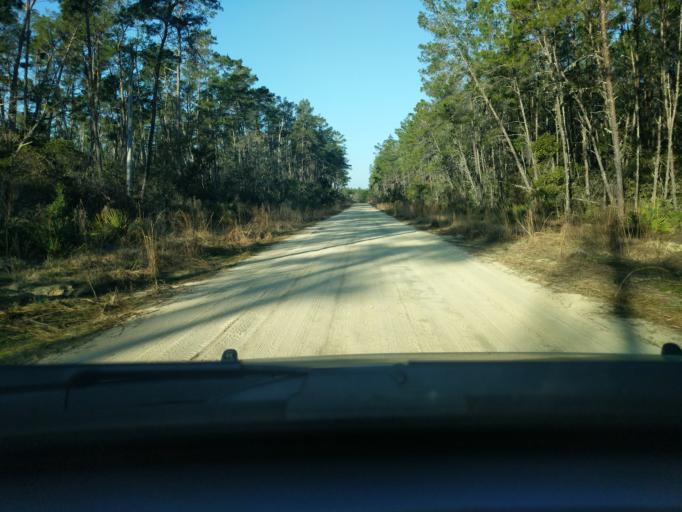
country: US
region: Florida
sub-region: Marion County
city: Silver Springs Shores
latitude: 29.2264
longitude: -81.8241
